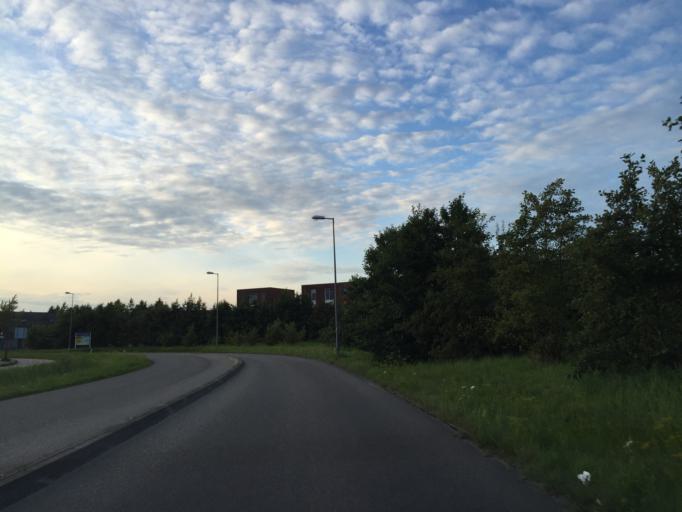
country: NL
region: South Holland
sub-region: Gemeente Rijnwoude
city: Benthuizen
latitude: 52.0692
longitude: 4.5277
